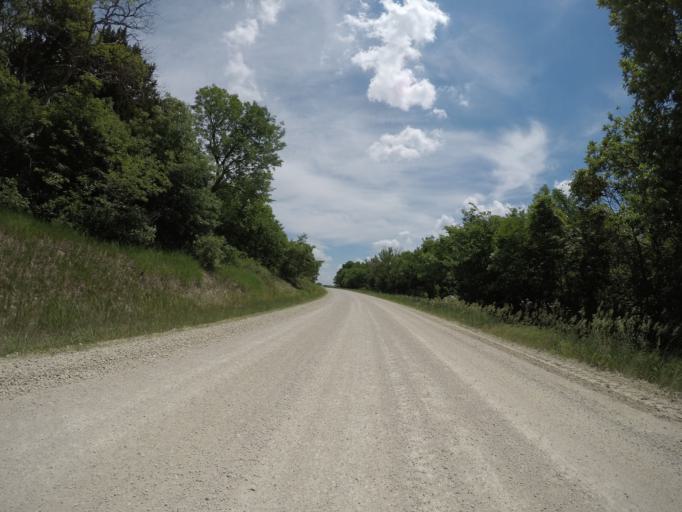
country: US
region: Kansas
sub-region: Wabaunsee County
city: Alma
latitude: 38.9168
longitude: -96.2171
